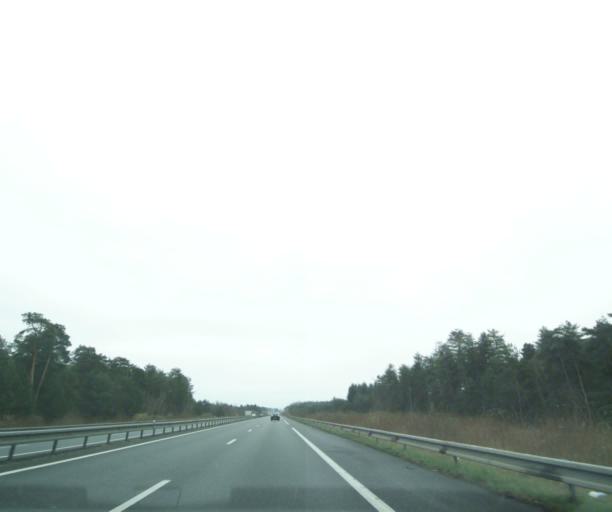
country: FR
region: Centre
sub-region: Departement du Loir-et-Cher
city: Lamotte-Beuvron
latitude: 47.5884
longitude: 1.9898
